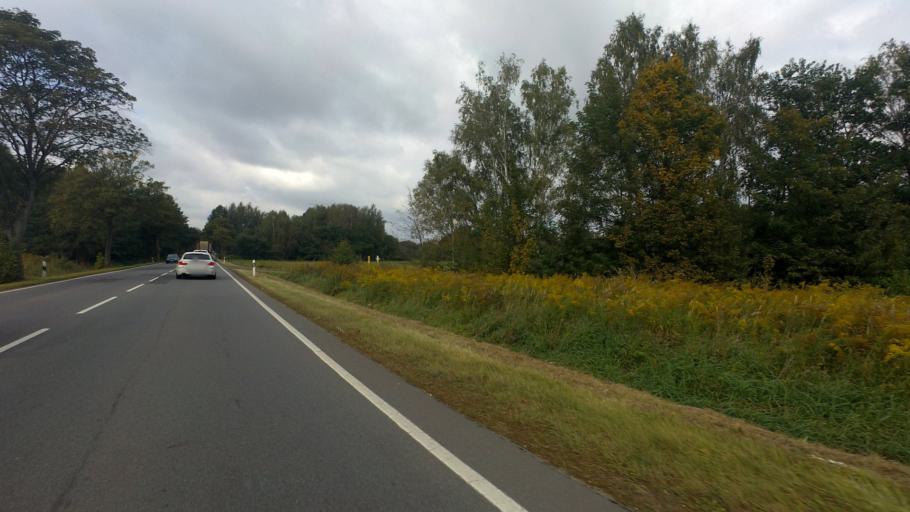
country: DE
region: Brandenburg
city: Schwarzheide
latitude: 51.4684
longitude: 13.8567
